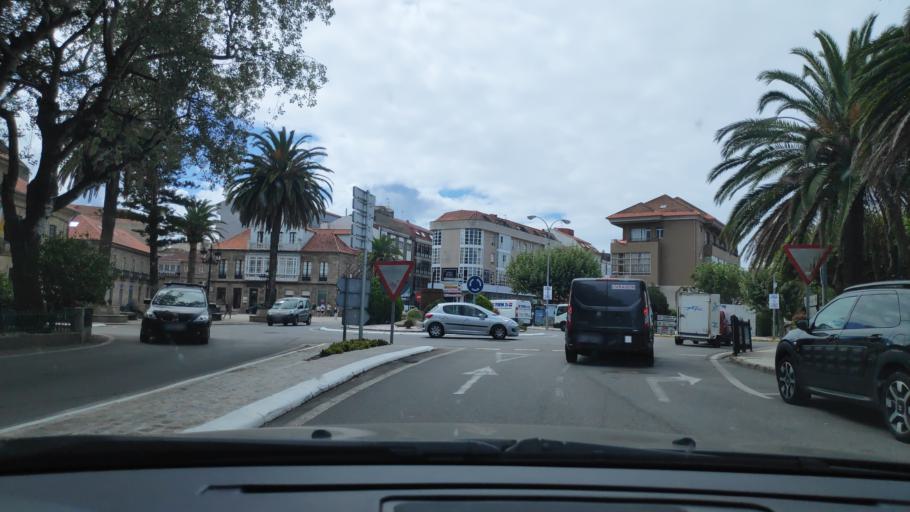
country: ES
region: Galicia
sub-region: Provincia de Pontevedra
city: Cambados
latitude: 42.5159
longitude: -8.8150
